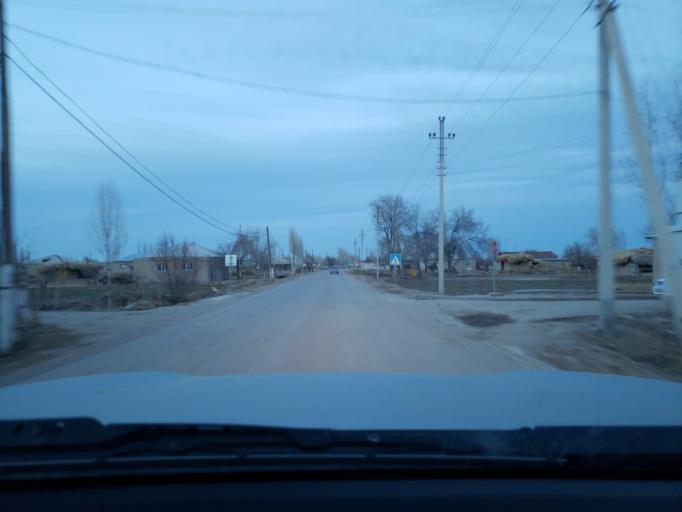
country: TM
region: Dasoguz
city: Tagta
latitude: 41.6318
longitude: 60.0678
